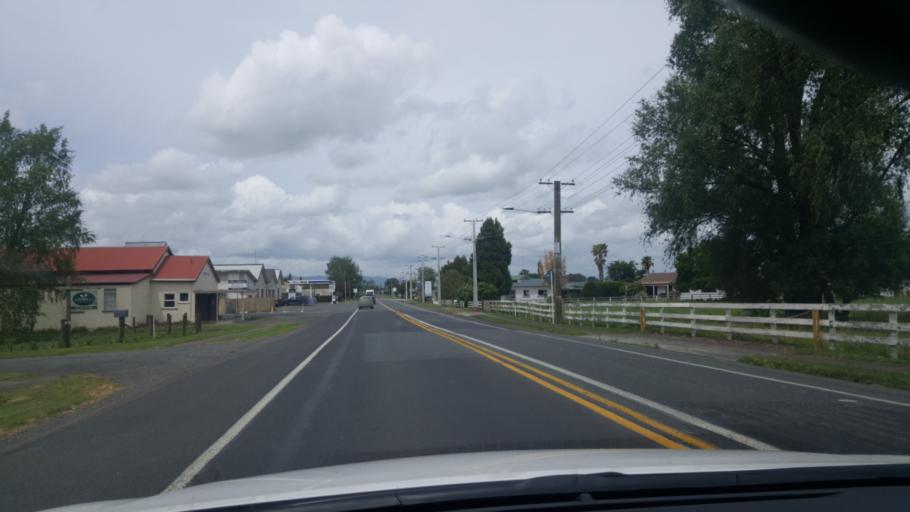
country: NZ
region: Waikato
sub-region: Matamata-Piako District
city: Matamata
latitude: -37.8823
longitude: 175.7603
